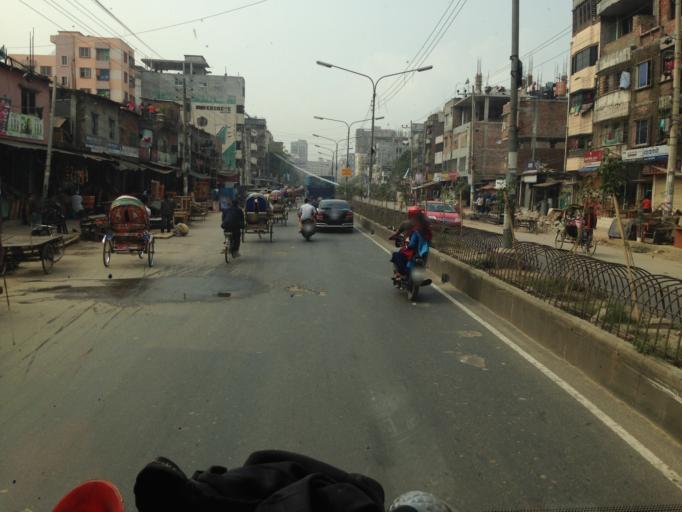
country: BD
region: Dhaka
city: Tungi
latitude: 23.8214
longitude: 90.3719
